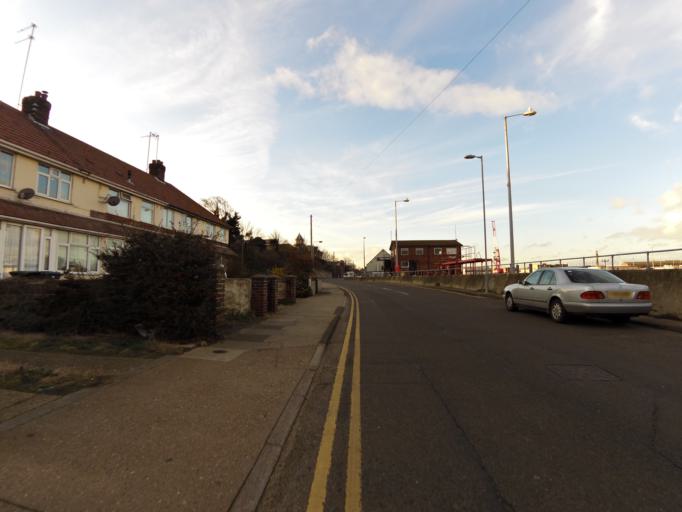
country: GB
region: England
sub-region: Norfolk
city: Gorleston-on-Sea
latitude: 52.5822
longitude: 1.7300
